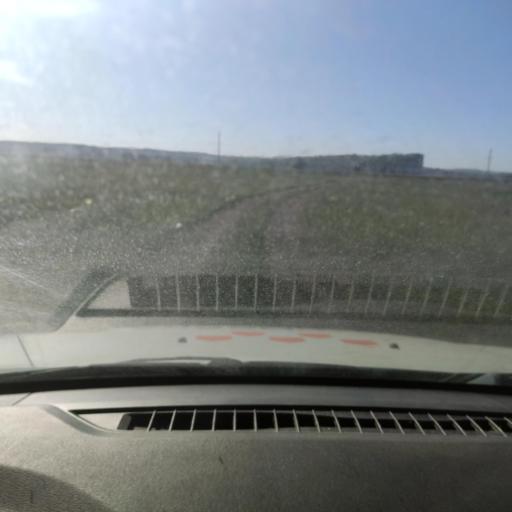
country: RU
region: Bashkortostan
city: Mikhaylovka
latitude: 54.9640
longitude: 55.7647
